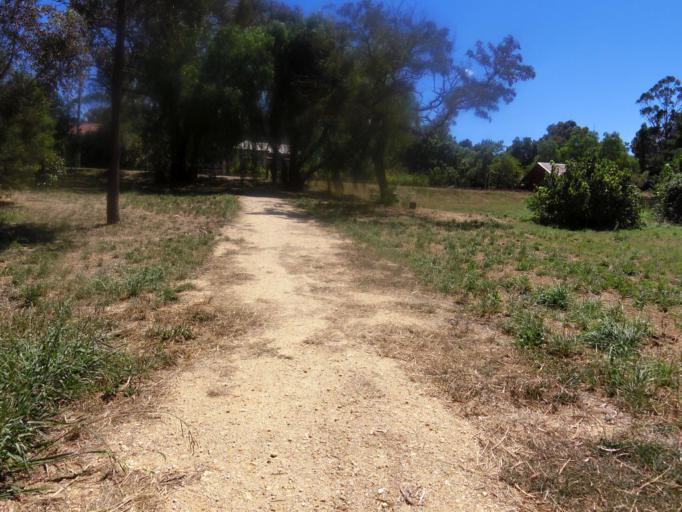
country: AU
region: Victoria
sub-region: Mount Alexander
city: Castlemaine
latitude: -36.9937
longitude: 144.0729
